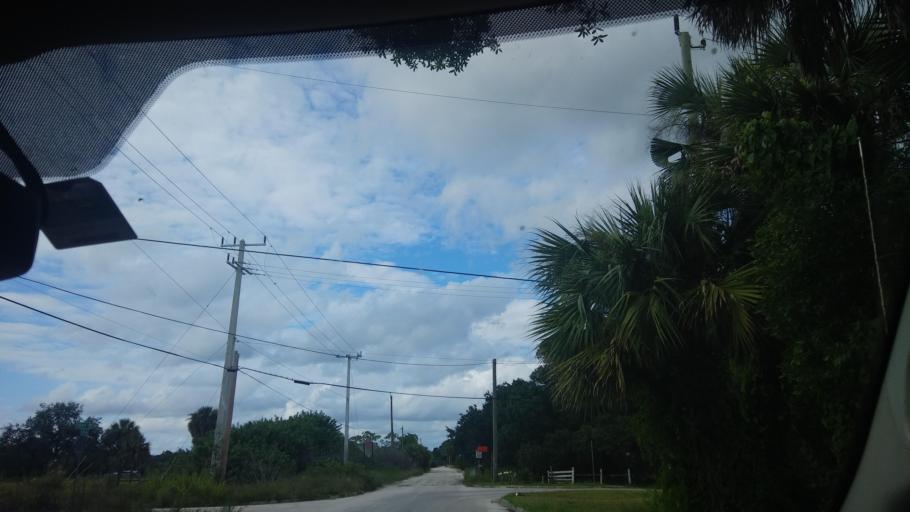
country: US
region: Florida
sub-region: Indian River County
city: Fellsmere
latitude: 27.7789
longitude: -80.5930
